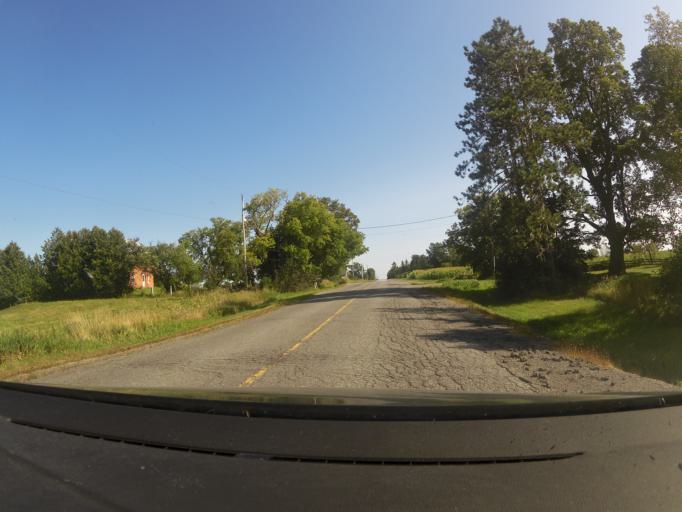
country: CA
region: Ontario
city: Arnprior
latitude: 45.3846
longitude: -76.1325
